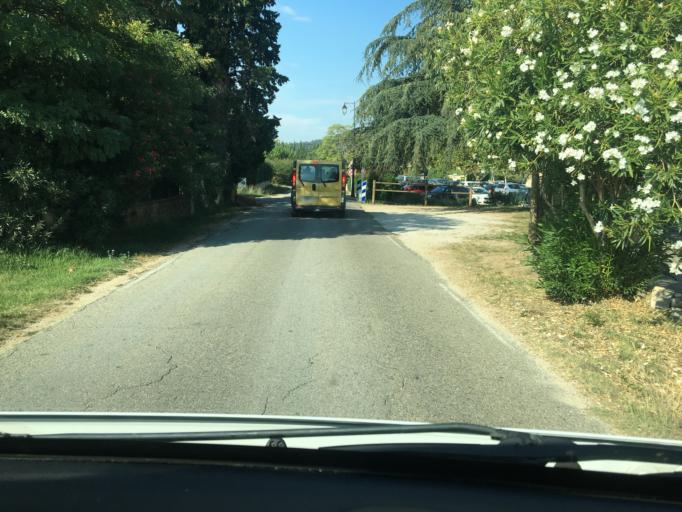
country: FR
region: Languedoc-Roussillon
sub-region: Departement du Gard
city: Saint-Julien-de-Peyrolas
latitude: 44.3010
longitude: 4.5548
